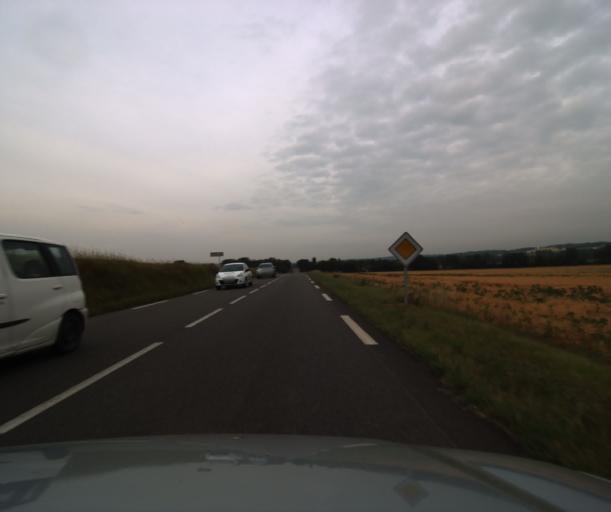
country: FR
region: Midi-Pyrenees
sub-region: Departement du Gers
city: Aubiet
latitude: 43.6702
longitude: 0.8033
